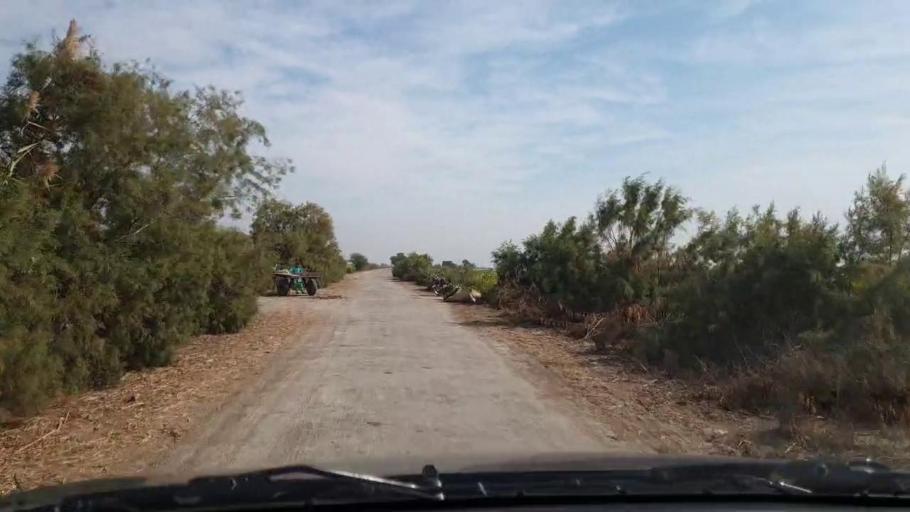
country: PK
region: Sindh
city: Jam Sahib
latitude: 26.2689
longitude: 68.6949
